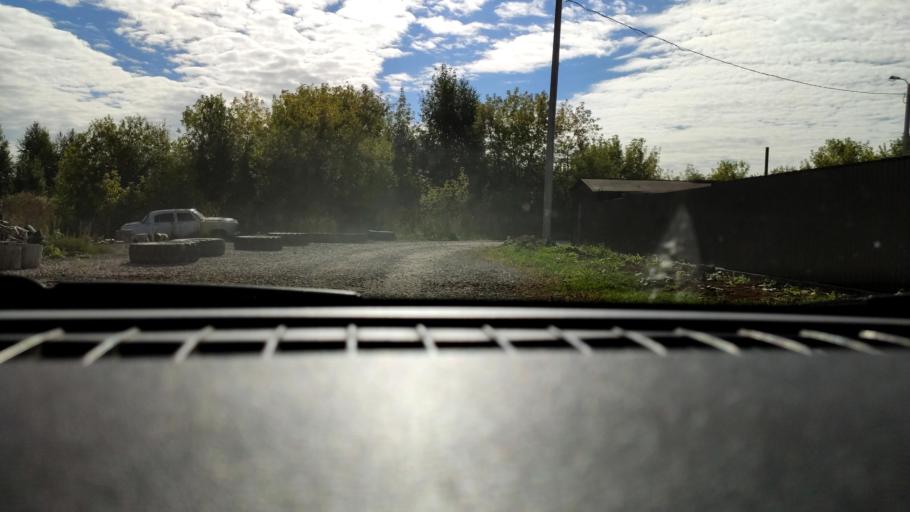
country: RU
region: Perm
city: Perm
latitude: 58.0152
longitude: 56.3378
